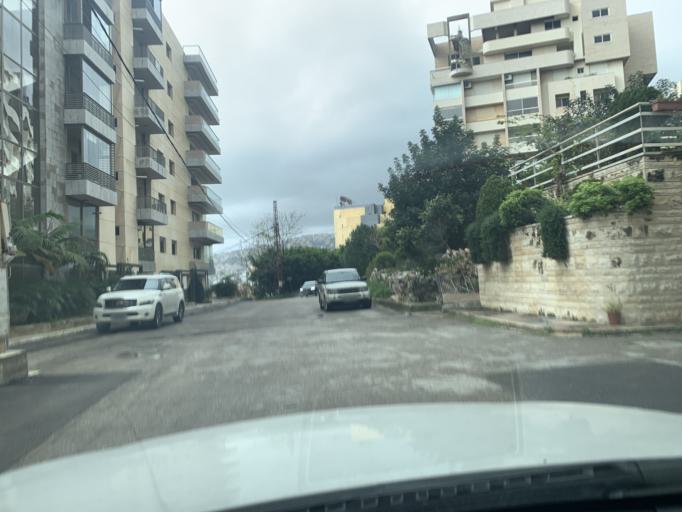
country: LB
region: Mont-Liban
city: Djounie
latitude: 34.0007
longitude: 35.6519
